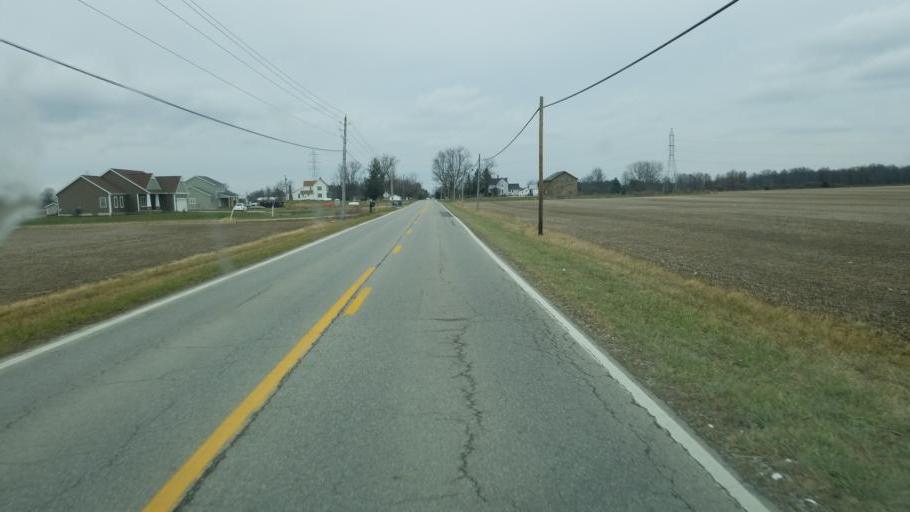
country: US
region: Ohio
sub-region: Delaware County
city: Delaware
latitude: 40.2377
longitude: -83.1315
